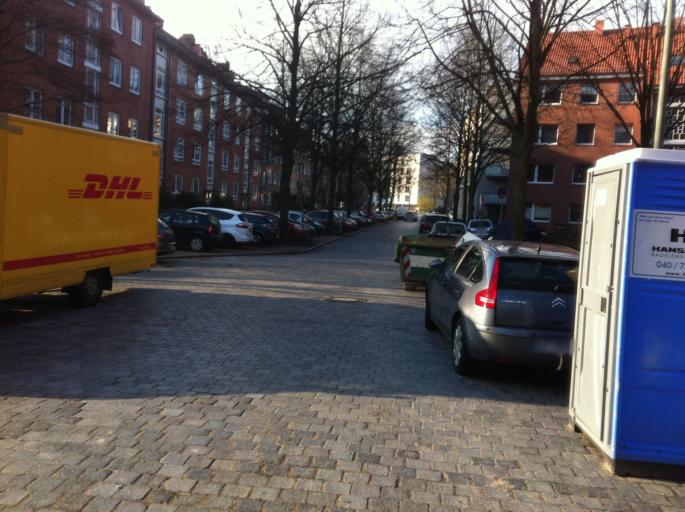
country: DE
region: Hamburg
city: St. Pauli
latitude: 53.5714
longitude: 9.9496
